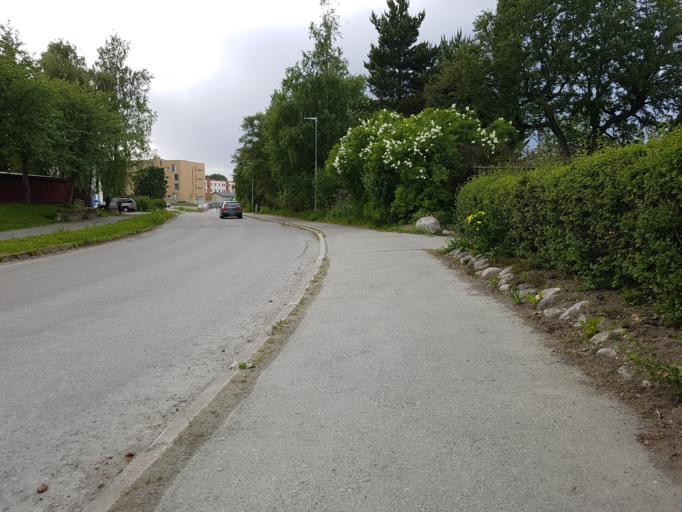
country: NO
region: Sor-Trondelag
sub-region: Trondheim
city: Trondheim
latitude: 63.4293
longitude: 10.4535
